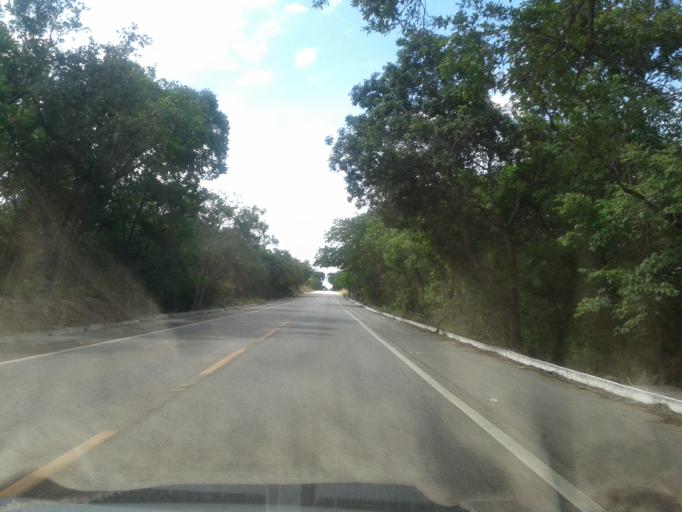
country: BR
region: Goias
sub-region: Itapuranga
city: Itapuranga
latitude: -15.4740
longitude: -50.3412
